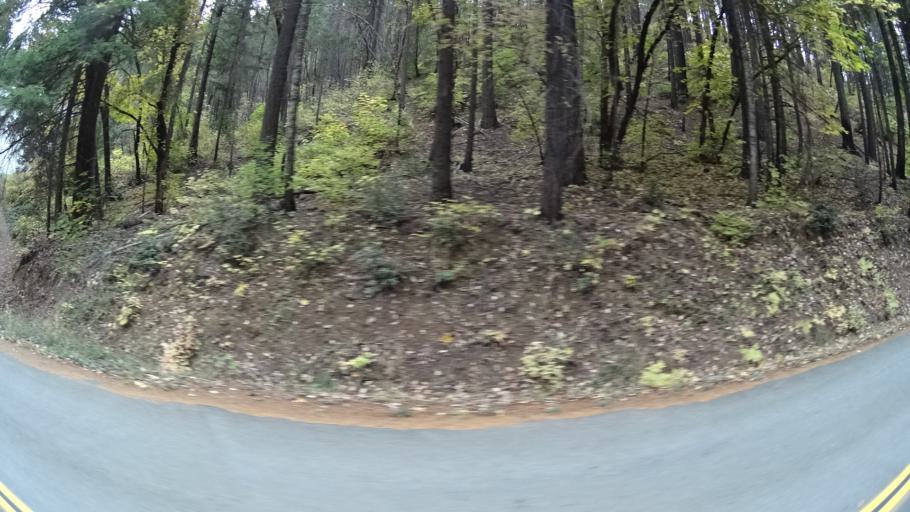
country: US
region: California
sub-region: Siskiyou County
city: Happy Camp
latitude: 41.7840
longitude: -123.3878
